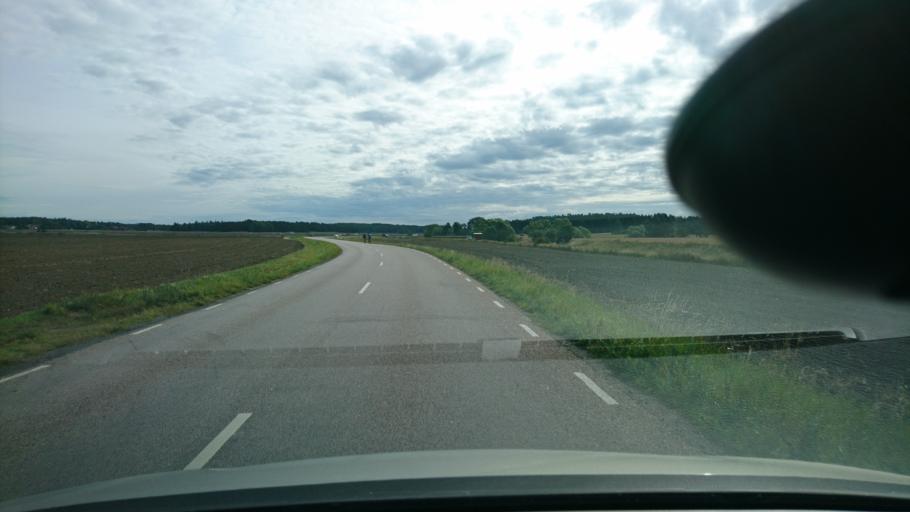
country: SE
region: Uppsala
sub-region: Uppsala Kommun
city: Saevja
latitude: 59.8267
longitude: 17.7239
